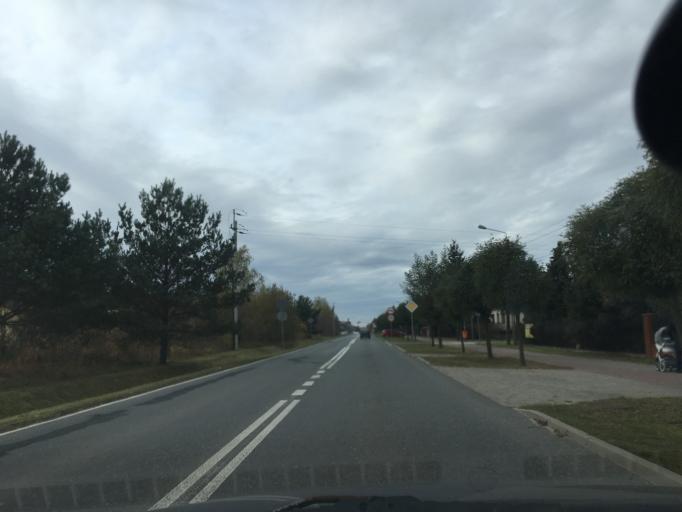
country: PL
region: Masovian Voivodeship
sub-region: Powiat zyrardowski
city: Mszczonow
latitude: 51.9737
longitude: 20.5343
